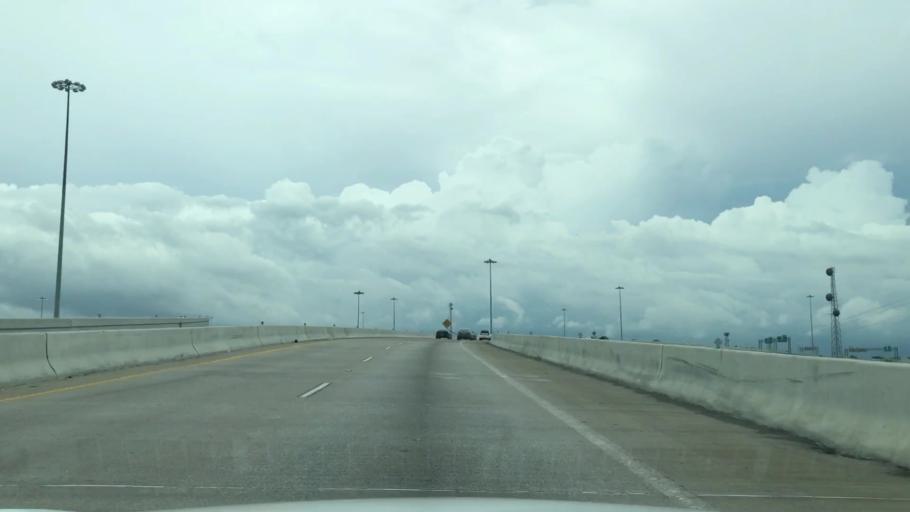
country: US
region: Texas
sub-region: Tarrant County
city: Fort Worth
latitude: 32.7500
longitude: -97.3206
